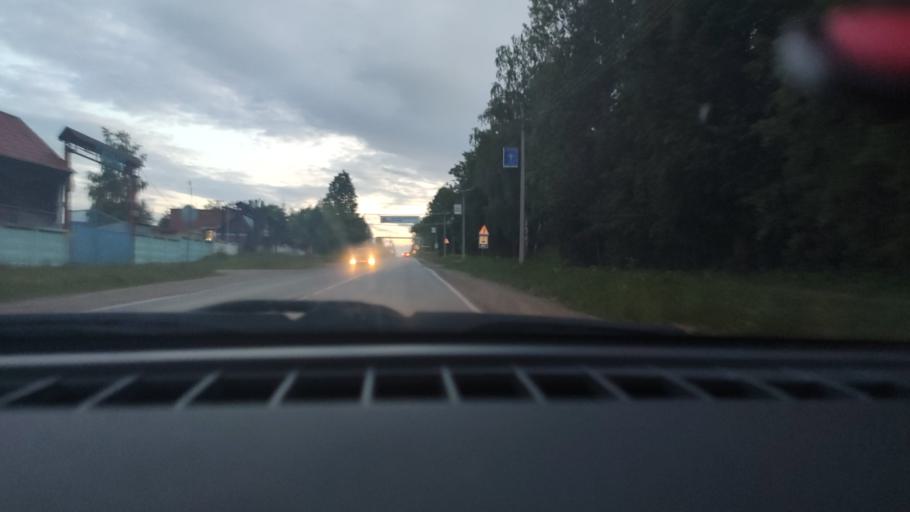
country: RU
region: Perm
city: Zvezdnyy
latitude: 57.7348
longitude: 56.3221
